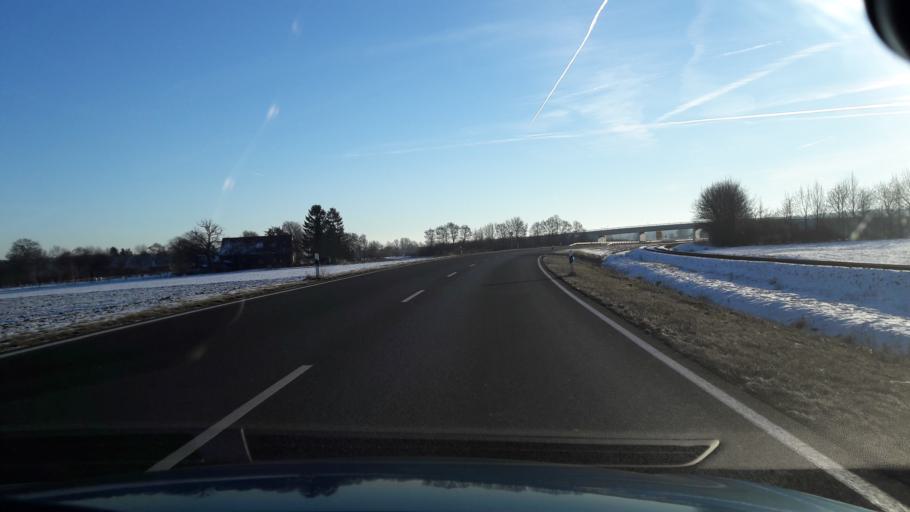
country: DE
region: North Rhine-Westphalia
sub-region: Regierungsbezirk Munster
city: Beckum
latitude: 51.7454
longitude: 8.1020
